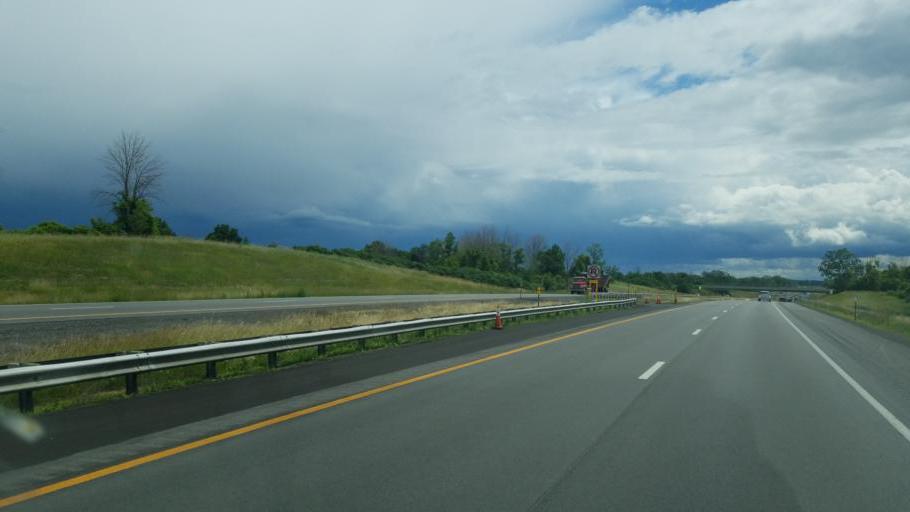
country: US
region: New York
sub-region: Monroe County
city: Scottsville
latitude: 43.0439
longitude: -77.7847
